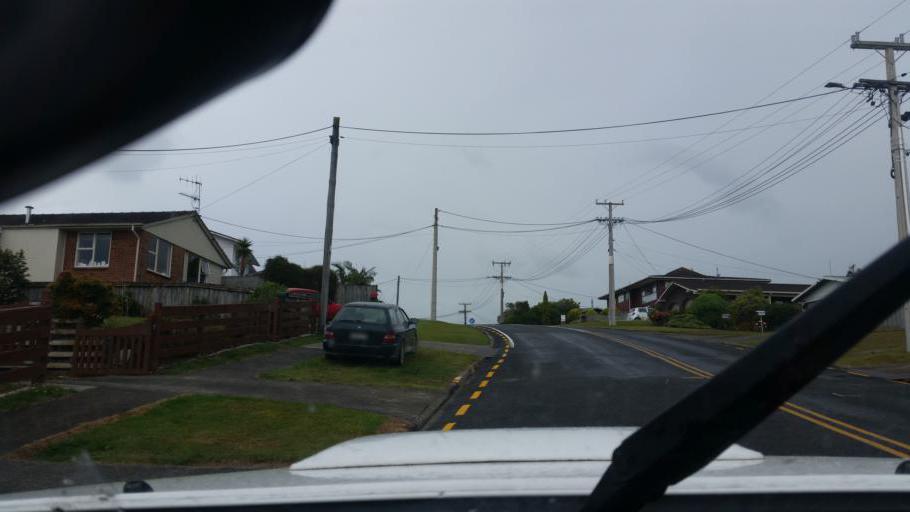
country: NZ
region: Northland
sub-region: Kaipara District
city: Dargaville
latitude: -35.9304
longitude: 173.8623
